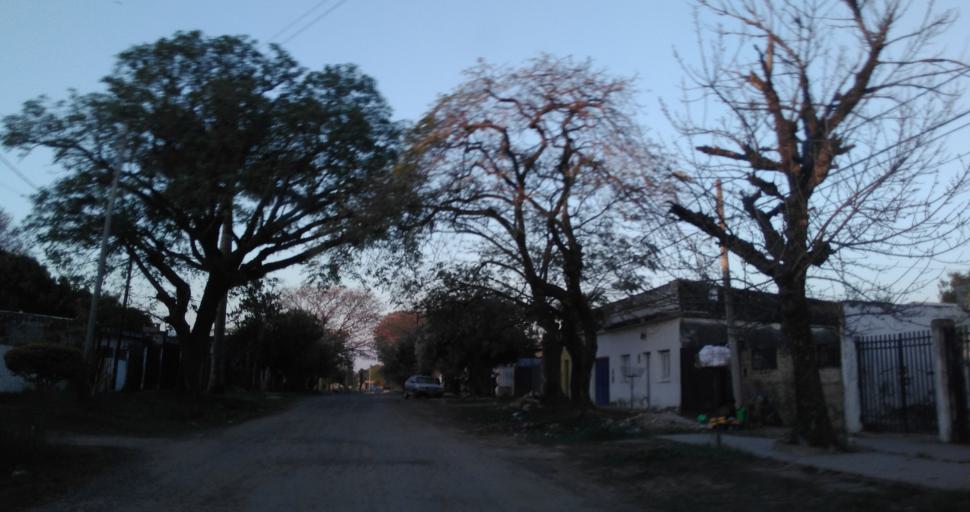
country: AR
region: Chaco
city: Resistencia
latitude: -27.4552
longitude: -58.9731
